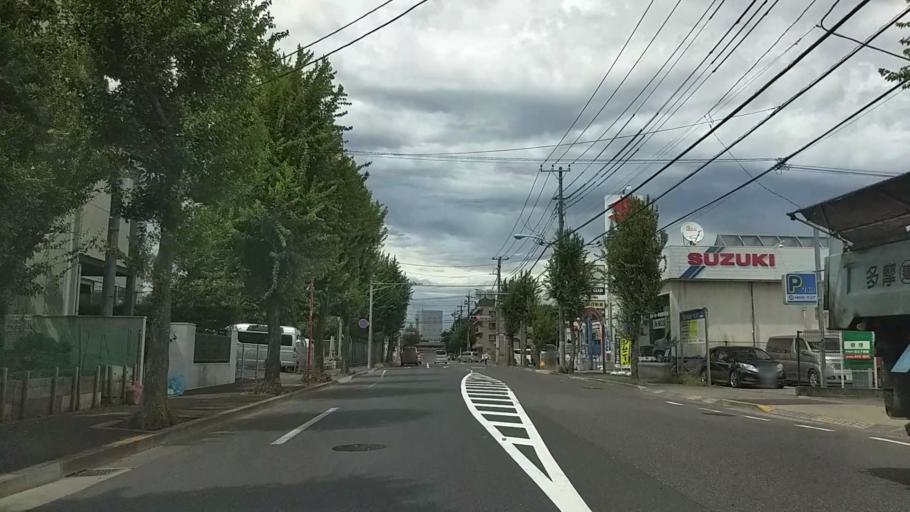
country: JP
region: Tokyo
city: Hachioji
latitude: 35.6471
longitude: 139.3596
